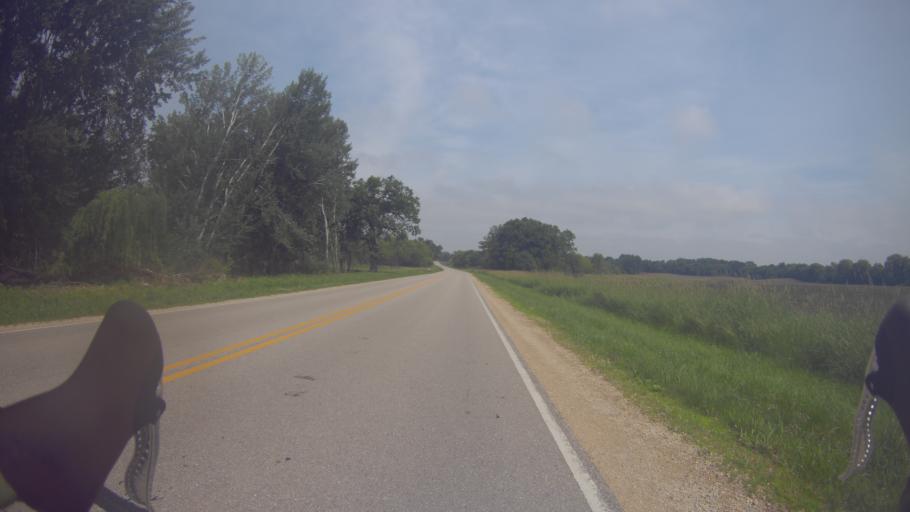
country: US
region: Wisconsin
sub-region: Rock County
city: Edgerton
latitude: 42.8669
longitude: -89.0329
